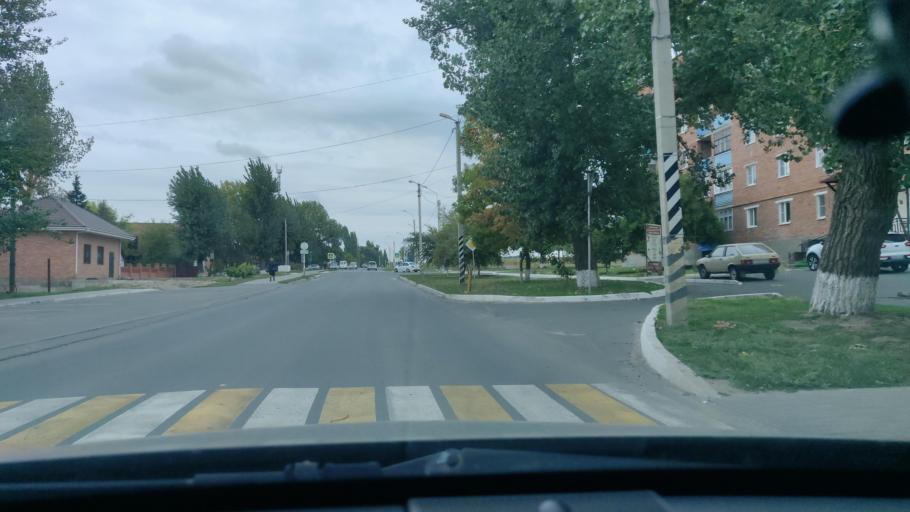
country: RU
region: Rostov
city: Ust'-Donetskiy
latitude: 47.6465
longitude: 40.8610
